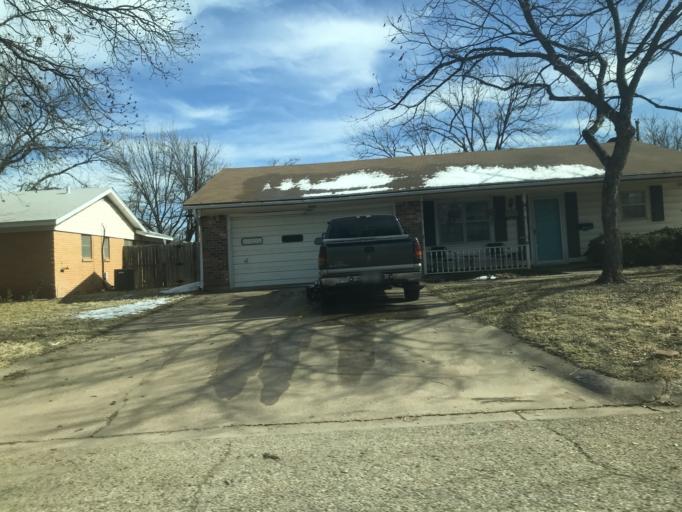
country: US
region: Texas
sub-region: Taylor County
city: Abilene
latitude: 32.4728
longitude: -99.7702
